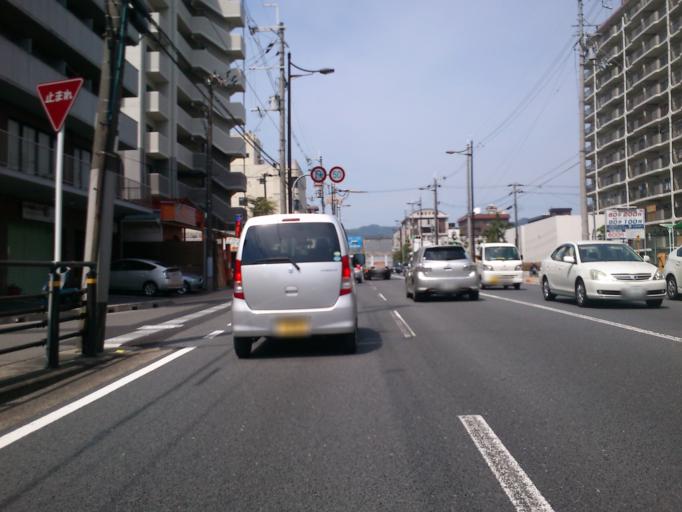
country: JP
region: Kyoto
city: Muko
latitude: 34.9961
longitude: 135.7226
